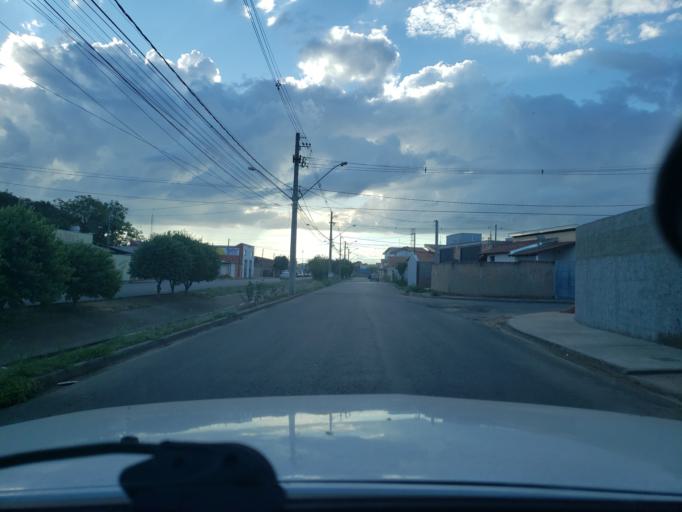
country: BR
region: Sao Paulo
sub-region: Moji-Guacu
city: Mogi-Gaucu
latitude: -22.3298
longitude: -46.9257
